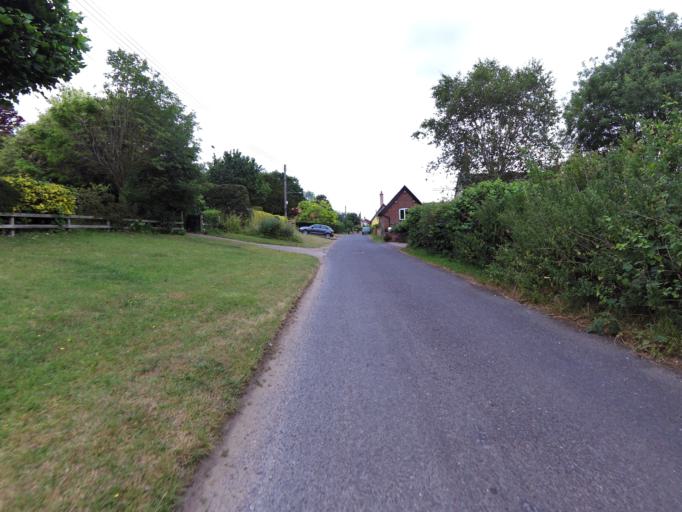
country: GB
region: England
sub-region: Norfolk
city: Harleston
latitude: 52.4087
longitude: 1.3400
